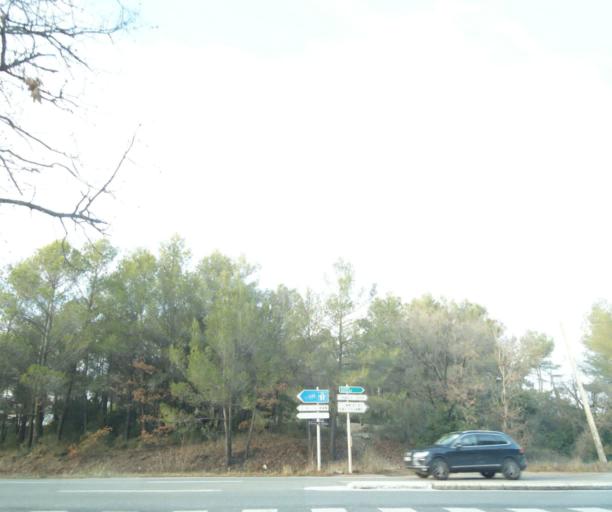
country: FR
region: Provence-Alpes-Cote d'Azur
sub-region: Departement du Var
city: La Motte
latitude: 43.5234
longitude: 6.5366
